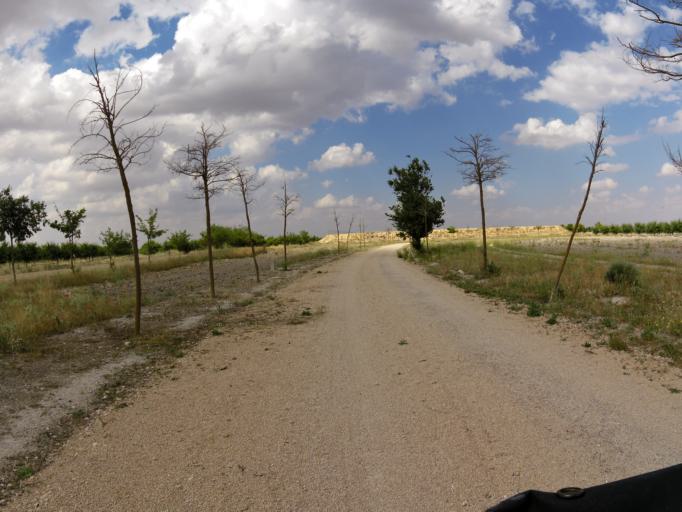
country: ES
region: Castille-La Mancha
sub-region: Provincia de Albacete
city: Albacete
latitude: 38.9557
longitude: -1.9786
